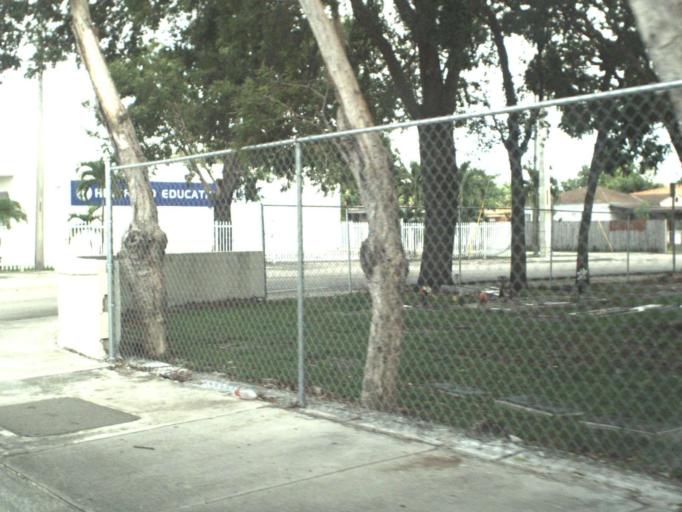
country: US
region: Florida
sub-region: Miami-Dade County
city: West Miami
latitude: 25.7710
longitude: -80.2853
